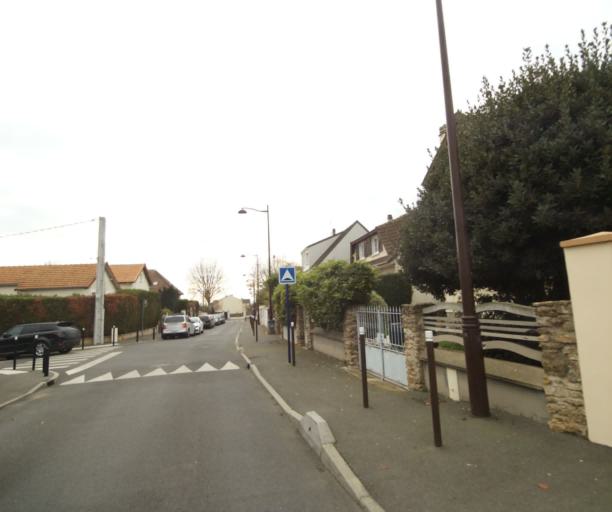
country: FR
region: Ile-de-France
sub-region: Departement du Val-d'Oise
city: Arnouville
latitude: 48.9861
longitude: 2.4265
